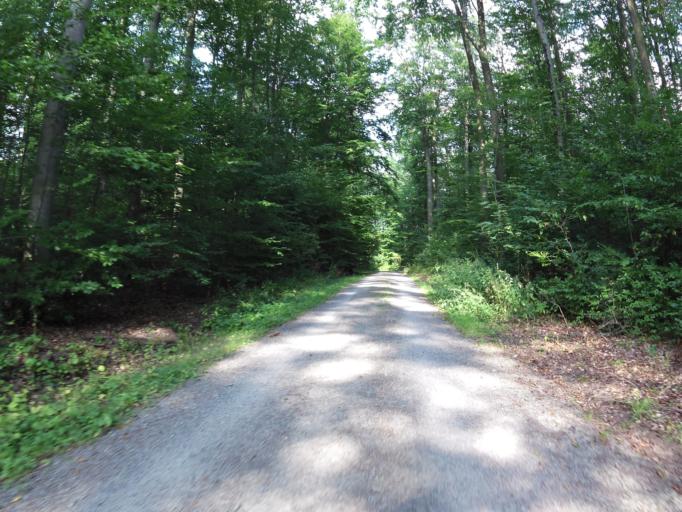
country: DE
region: Bavaria
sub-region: Regierungsbezirk Unterfranken
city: Kleinrinderfeld
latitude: 49.7180
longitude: 9.8333
